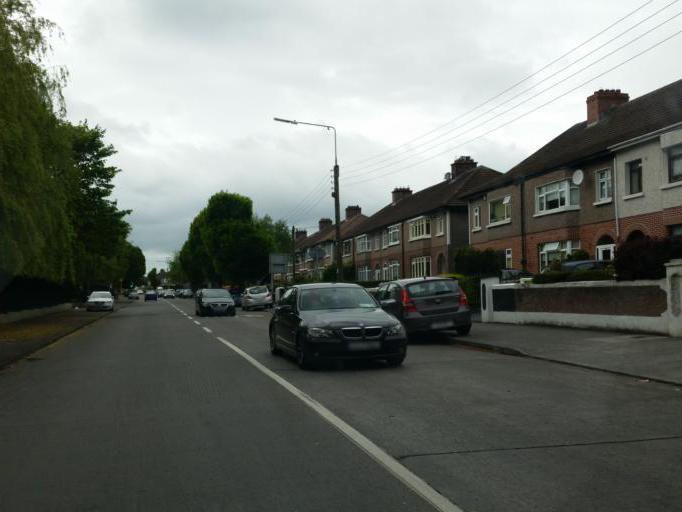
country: IE
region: Leinster
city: Cabra
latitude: 53.3673
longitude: -6.3029
